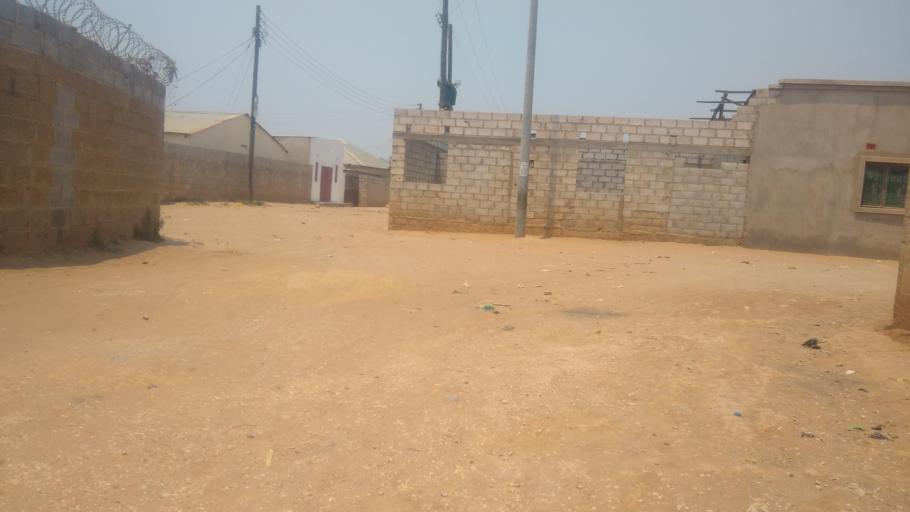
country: ZM
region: Lusaka
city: Lusaka
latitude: -15.4390
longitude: 28.3778
